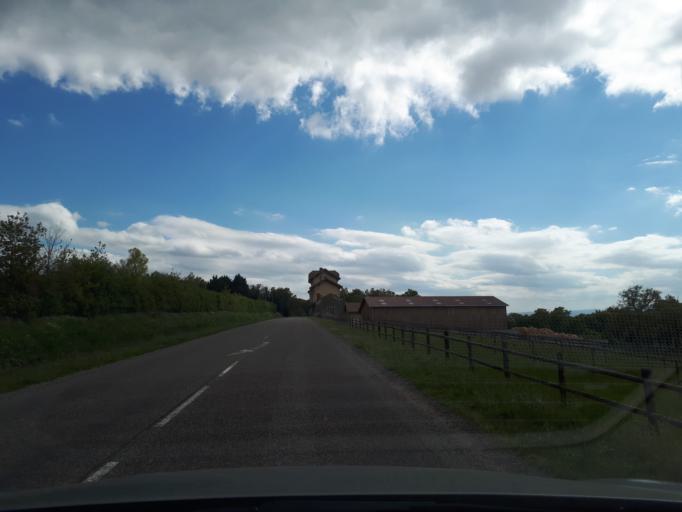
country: FR
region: Rhone-Alpes
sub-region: Departement de la Loire
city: Bellegarde-en-Forez
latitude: 45.6925
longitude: 4.3031
